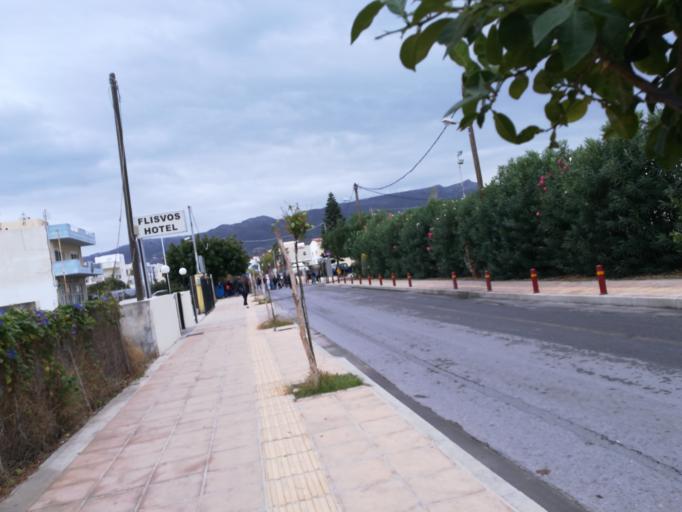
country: GR
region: Crete
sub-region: Nomos Lasithiou
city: Siteia
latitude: 35.2062
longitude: 26.1064
